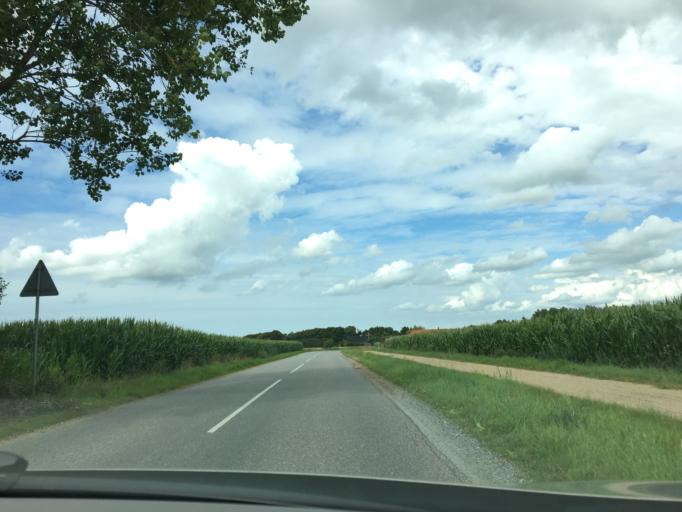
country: DK
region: South Denmark
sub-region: Varde Kommune
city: Oksbol
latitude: 55.6597
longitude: 8.2930
